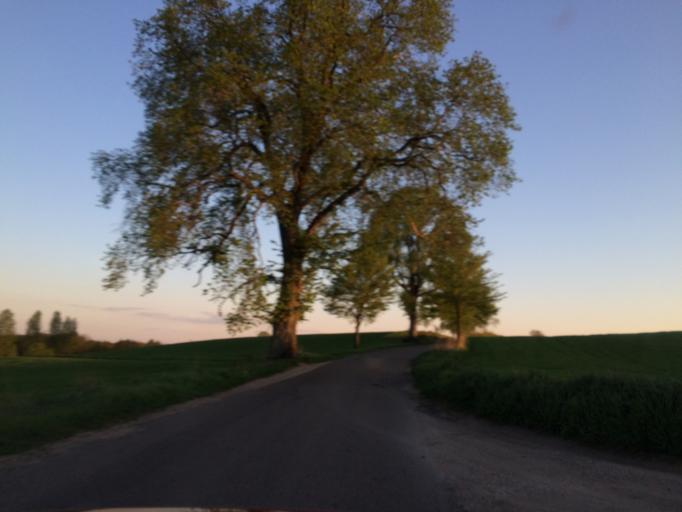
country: PL
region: Warmian-Masurian Voivodeship
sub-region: Powiat dzialdowski
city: Rybno
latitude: 53.4319
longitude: 19.9198
